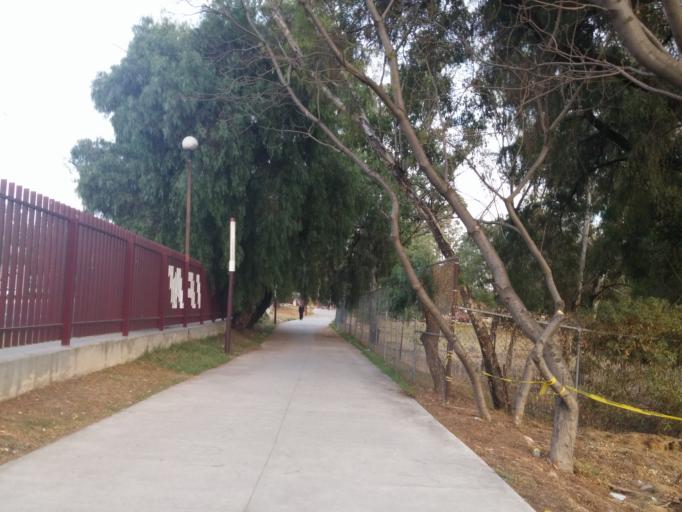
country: MX
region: Mexico
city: Colonia Lindavista
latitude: 19.5050
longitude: -99.1447
